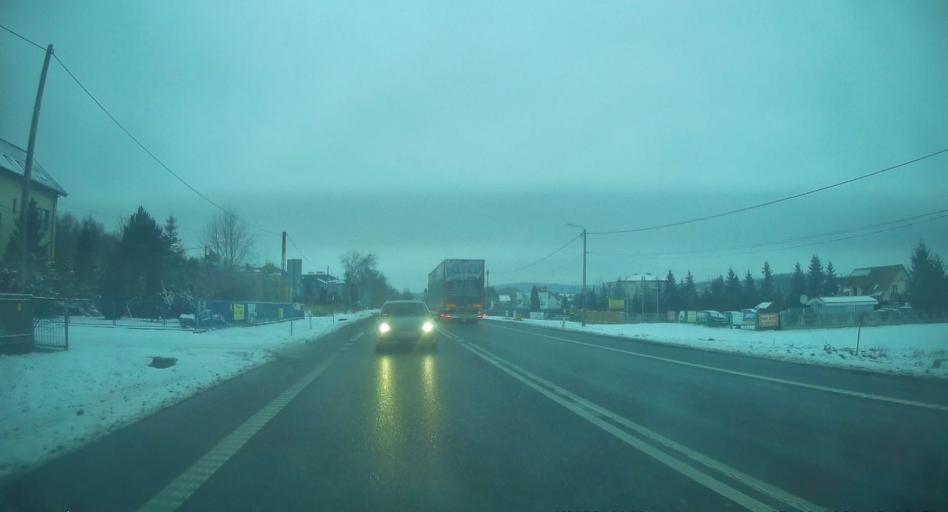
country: PL
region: Swietokrzyskie
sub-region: Powiat kielecki
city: Kostomloty Drugie
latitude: 50.9124
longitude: 20.5760
